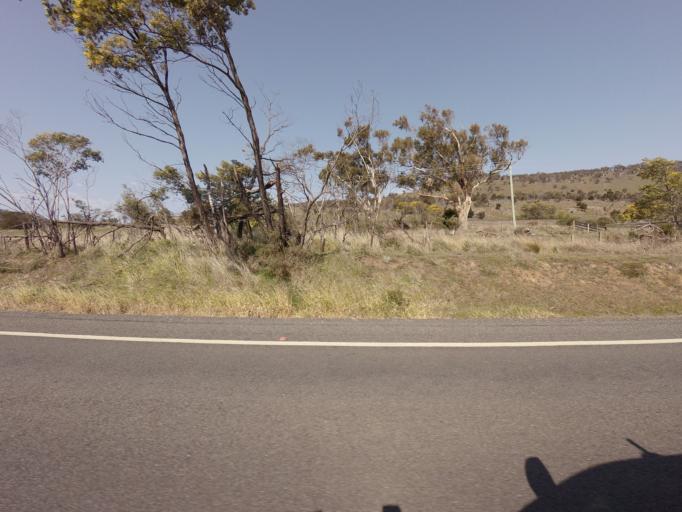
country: AU
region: Tasmania
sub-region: Northern Midlands
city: Evandale
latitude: -41.8160
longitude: 147.5740
